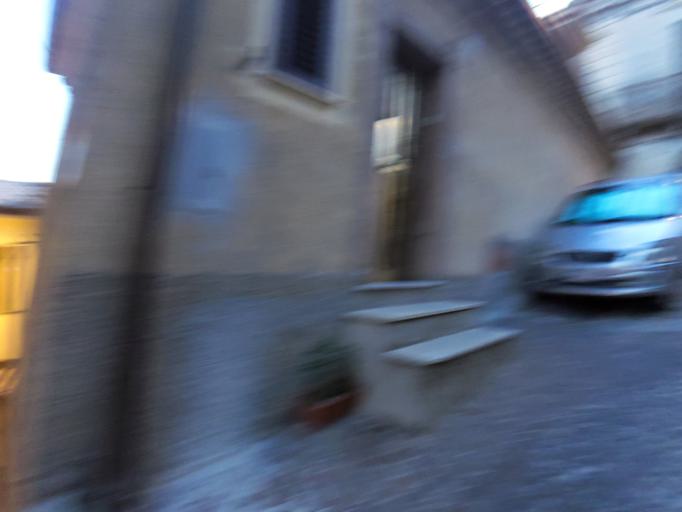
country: IT
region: Calabria
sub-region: Provincia di Reggio Calabria
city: Stilo
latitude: 38.4807
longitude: 16.4716
